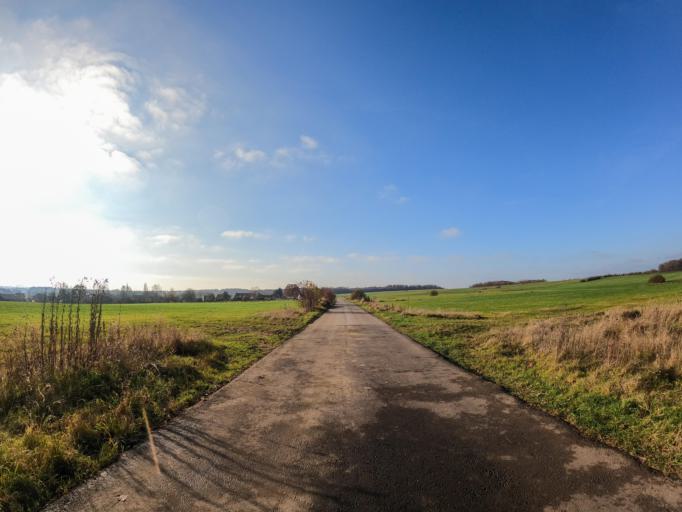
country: LU
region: Luxembourg
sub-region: Canton de Luxembourg
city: Olm
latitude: 49.6811
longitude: 6.0067
